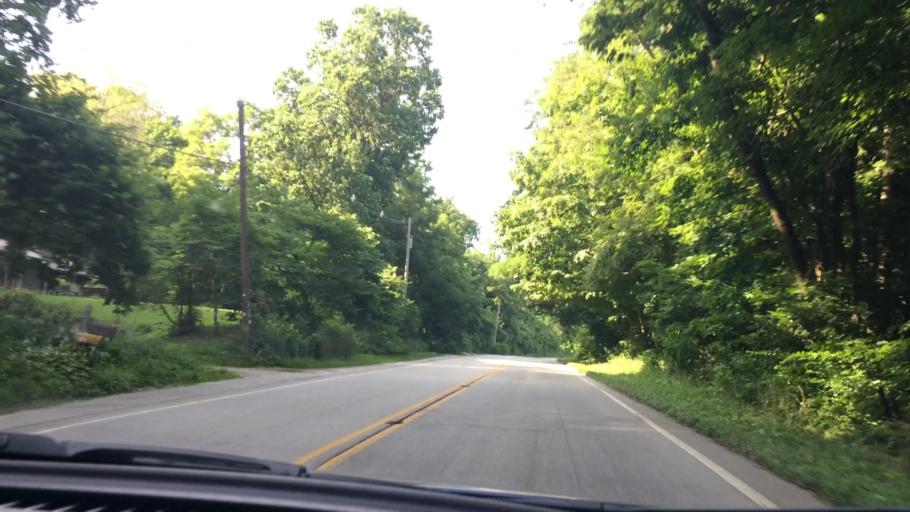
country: US
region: Indiana
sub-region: Tippecanoe County
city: Battle Ground
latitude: 40.4775
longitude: -86.8830
